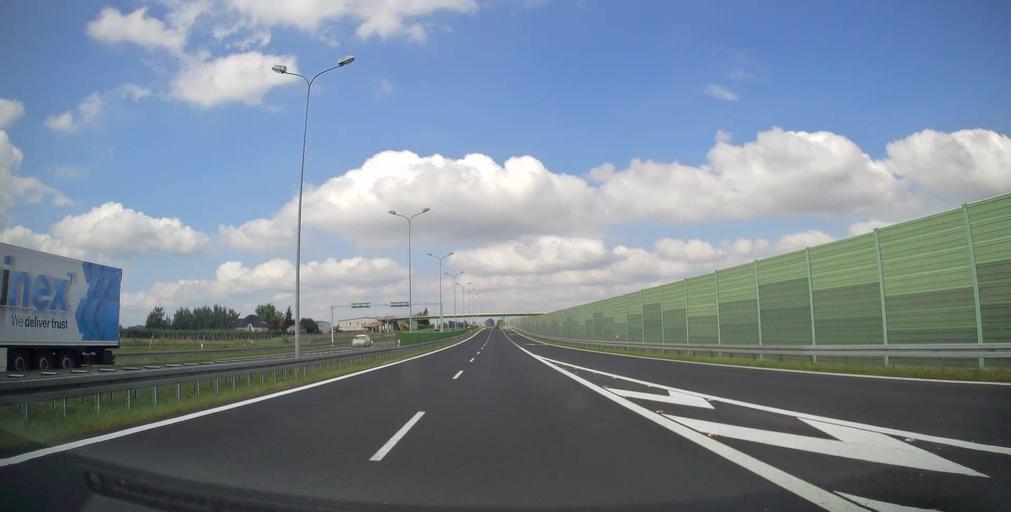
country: PL
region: Masovian Voivodeship
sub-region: Powiat grojecki
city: Grojec
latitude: 51.8364
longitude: 20.8767
